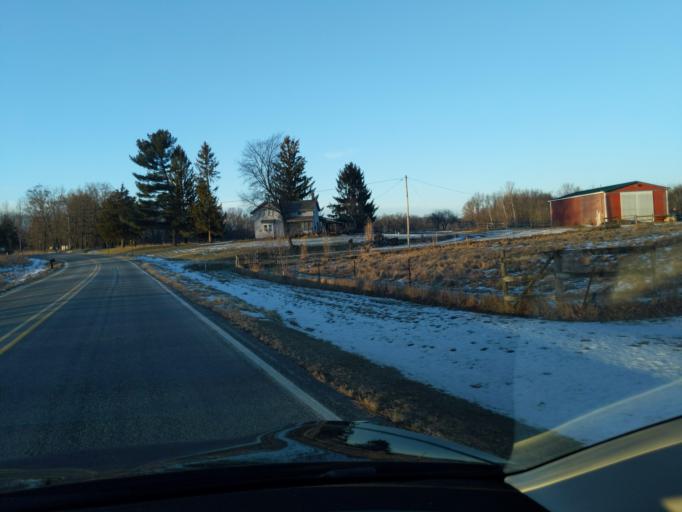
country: US
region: Michigan
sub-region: Ingham County
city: Stockbridge
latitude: 42.5064
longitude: -84.2569
